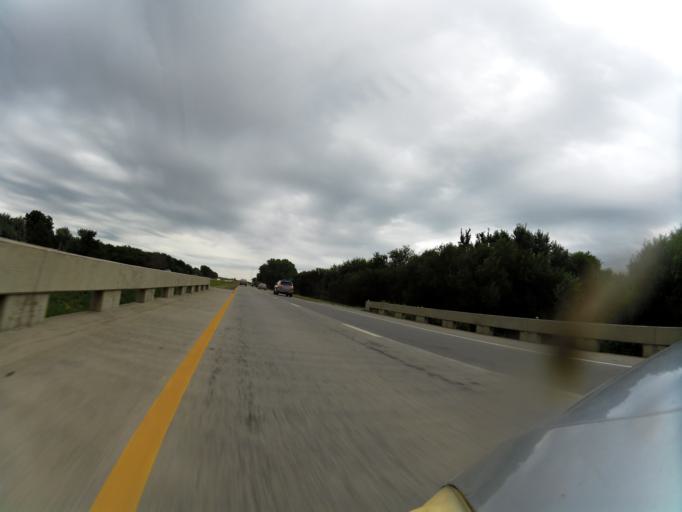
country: US
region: Kansas
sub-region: Sedgwick County
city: Maize
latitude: 37.7595
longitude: -97.4380
